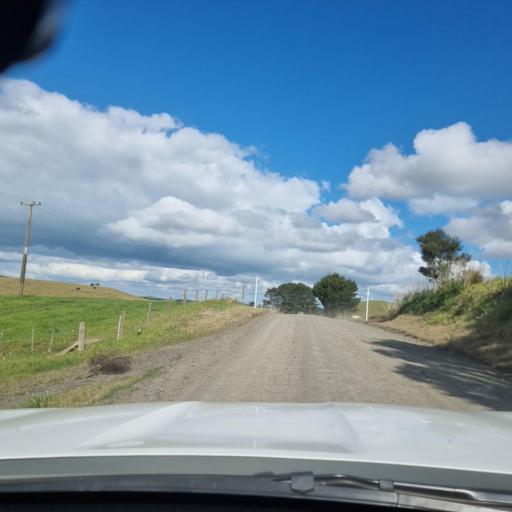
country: NZ
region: Auckland
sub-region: Auckland
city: Wellsford
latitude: -36.3196
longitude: 174.1345
